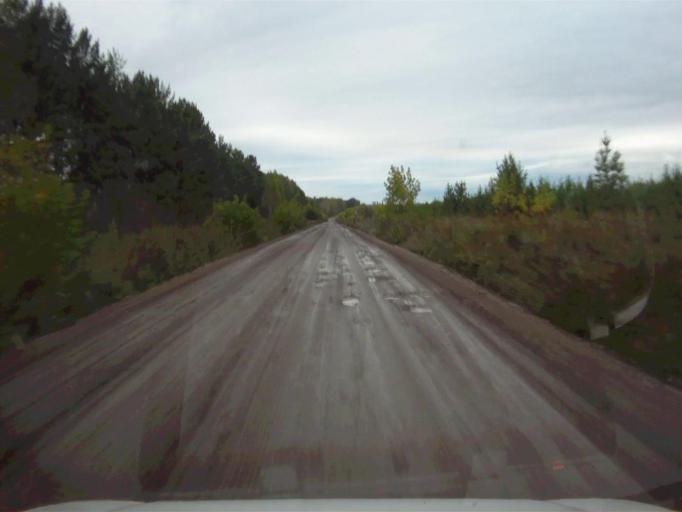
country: RU
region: Sverdlovsk
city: Mikhaylovsk
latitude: 56.1461
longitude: 59.2806
